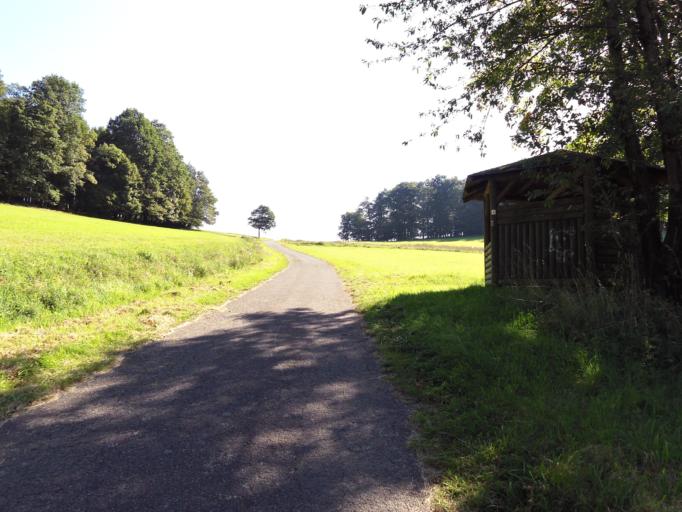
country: DE
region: Hesse
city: Lutzelbach
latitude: 49.7132
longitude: 8.7681
